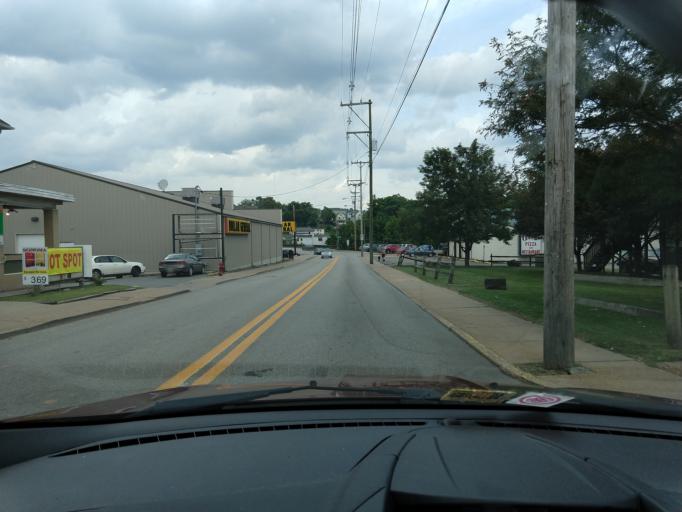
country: US
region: West Virginia
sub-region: Harrison County
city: Clarksburg
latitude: 39.2804
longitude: -80.3518
